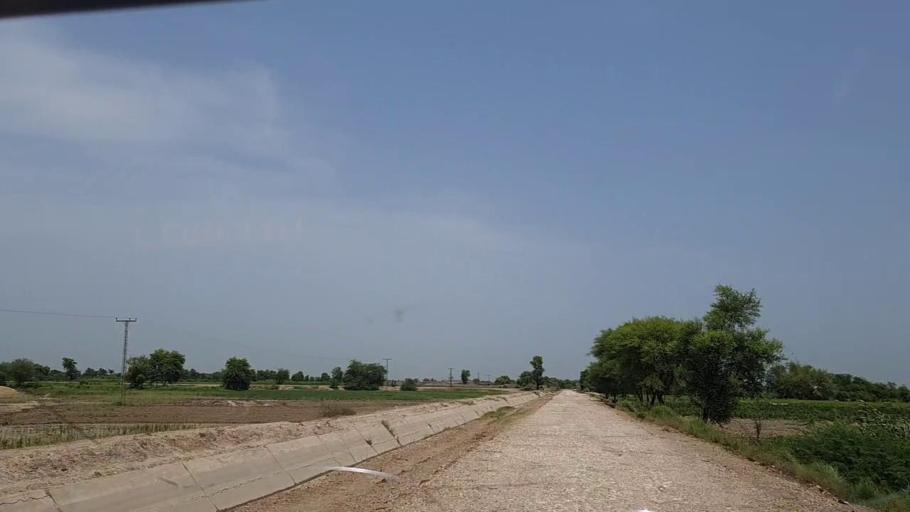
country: PK
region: Sindh
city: Tharu Shah
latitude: 26.9247
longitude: 68.0673
